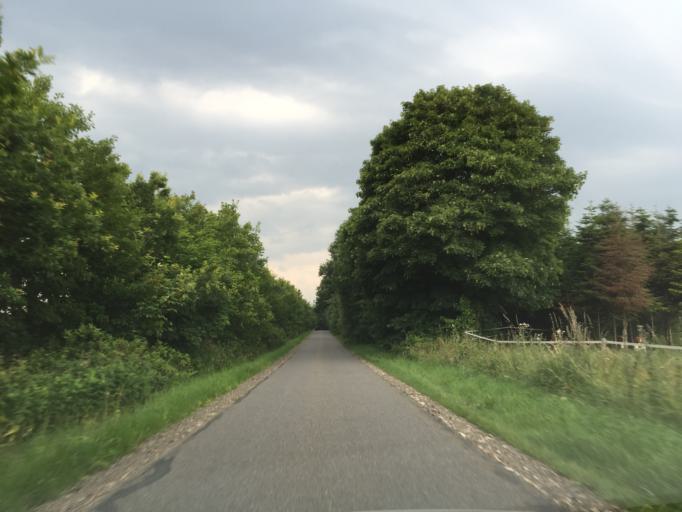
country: DK
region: Central Jutland
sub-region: Viborg Kommune
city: Bjerringbro
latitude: 56.3239
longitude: 9.6639
